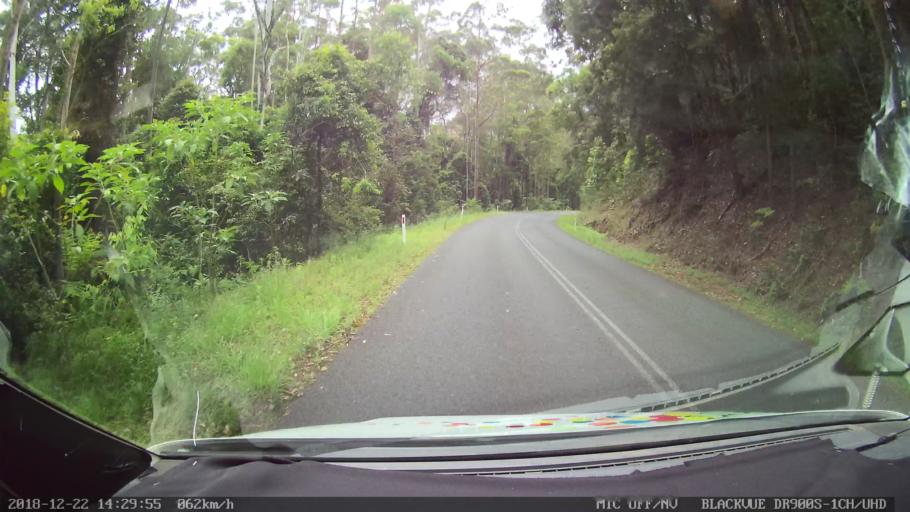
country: AU
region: New South Wales
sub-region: Bellingen
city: Dorrigo
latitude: -30.0809
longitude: 152.6339
